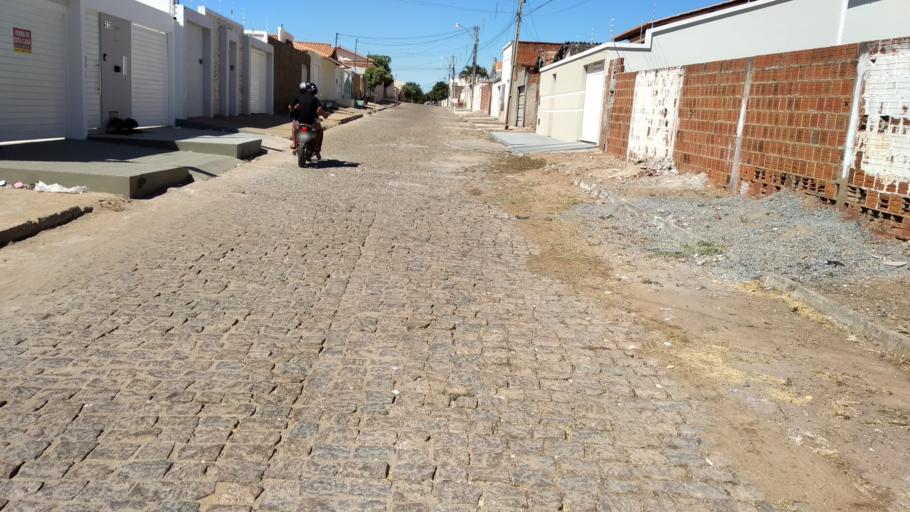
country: BR
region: Bahia
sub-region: Guanambi
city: Guanambi
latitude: -14.2348
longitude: -42.7755
